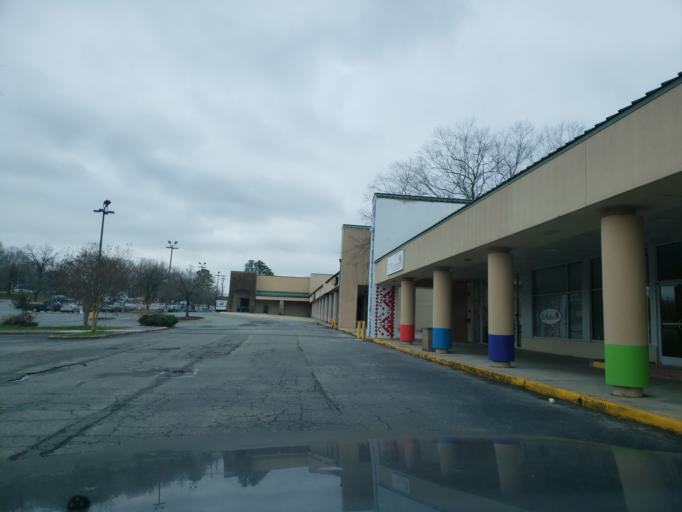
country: US
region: North Carolina
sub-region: Durham County
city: Durham
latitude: 35.9888
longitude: -78.9277
